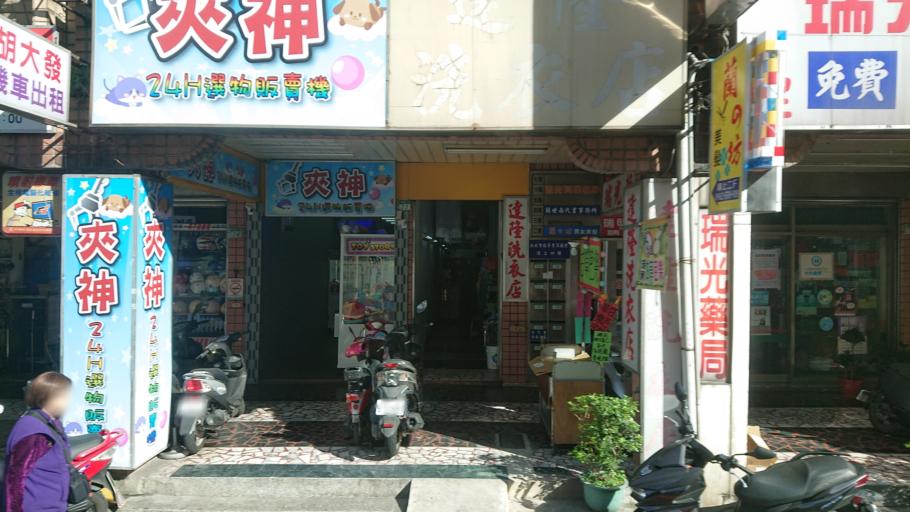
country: TW
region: Taiwan
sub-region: Keelung
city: Keelung
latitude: 25.1080
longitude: 121.8065
